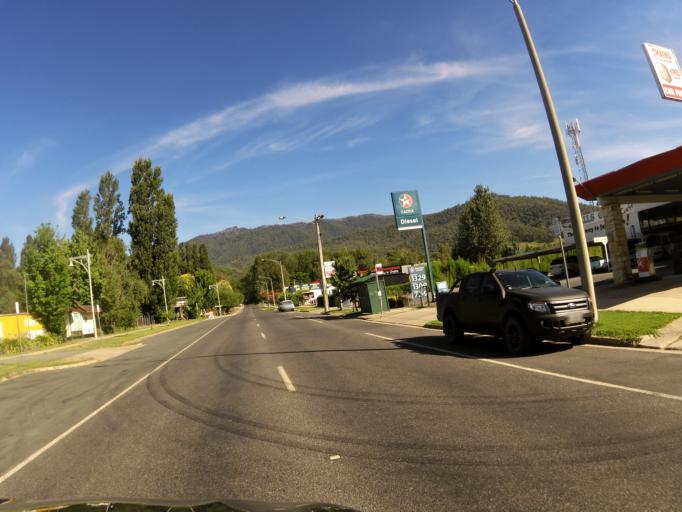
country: AU
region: Victoria
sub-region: Alpine
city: Mount Beauty
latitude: -36.7375
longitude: 147.1607
